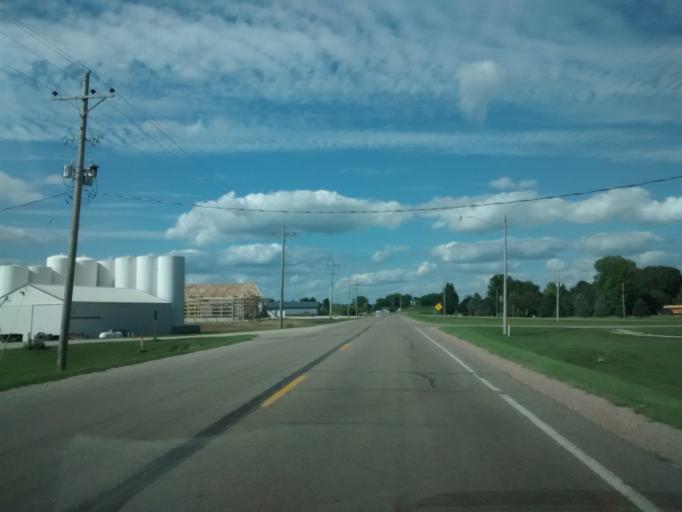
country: US
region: Iowa
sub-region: Woodbury County
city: Moville
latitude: 42.4923
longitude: -96.0735
